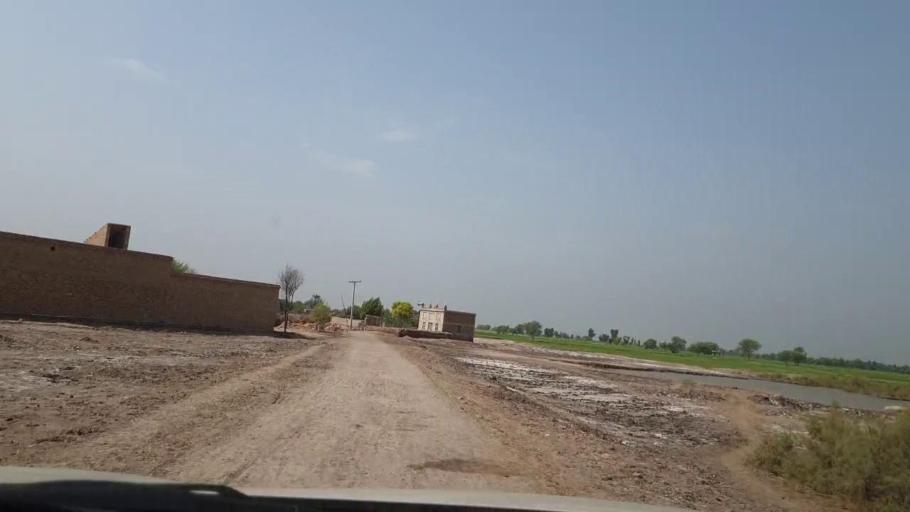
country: PK
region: Sindh
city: Dokri
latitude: 27.4168
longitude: 68.2037
